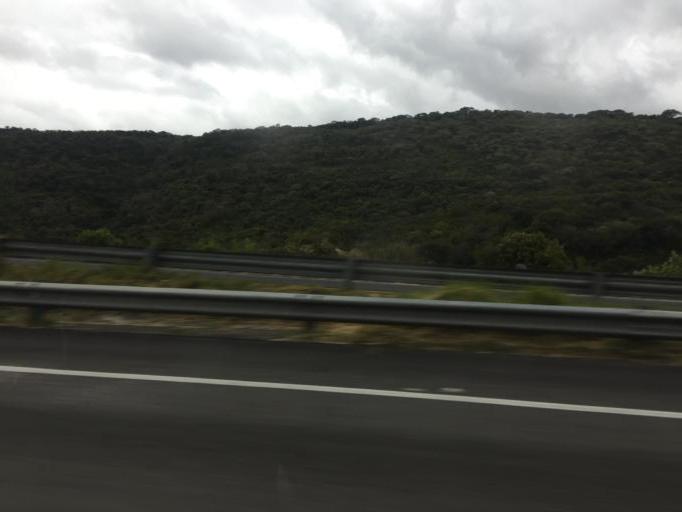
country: MX
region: Jalisco
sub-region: Zapotlan del Rey
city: Zapotlan del Rey
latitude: 20.5270
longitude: -103.0032
